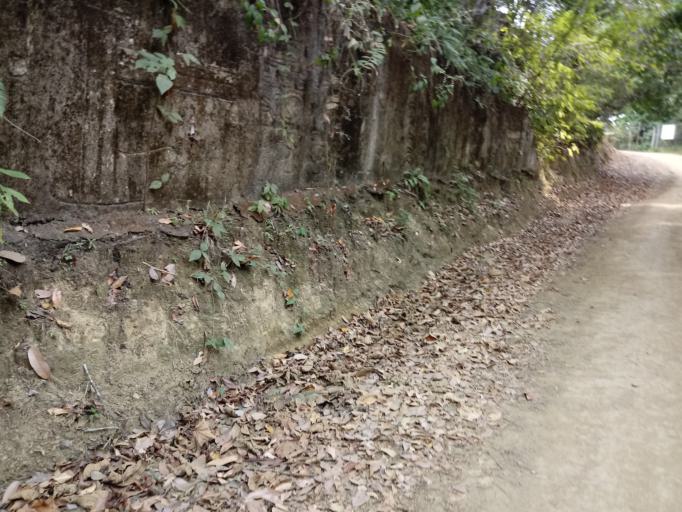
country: CR
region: Puntarenas
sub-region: Canton de Garabito
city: Jaco
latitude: 9.5948
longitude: -84.6179
